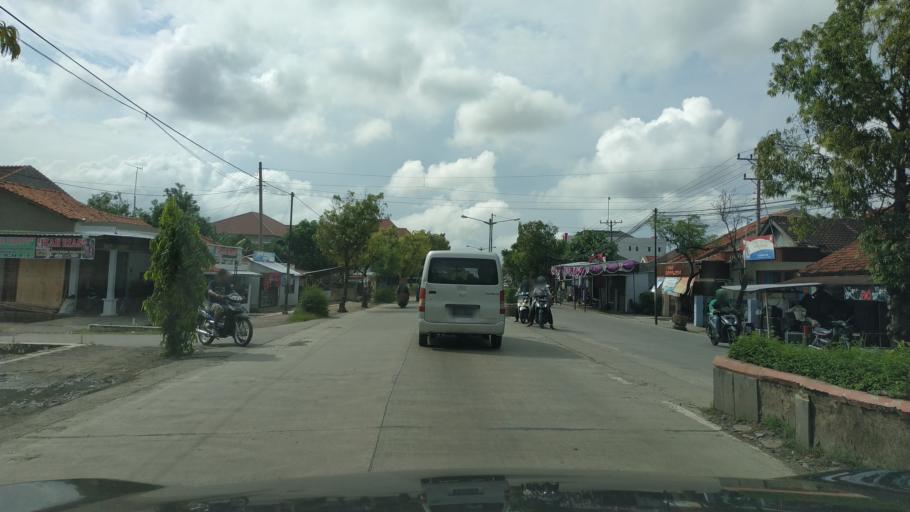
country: ID
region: Central Java
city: Pemalang
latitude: -6.9132
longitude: 109.3826
